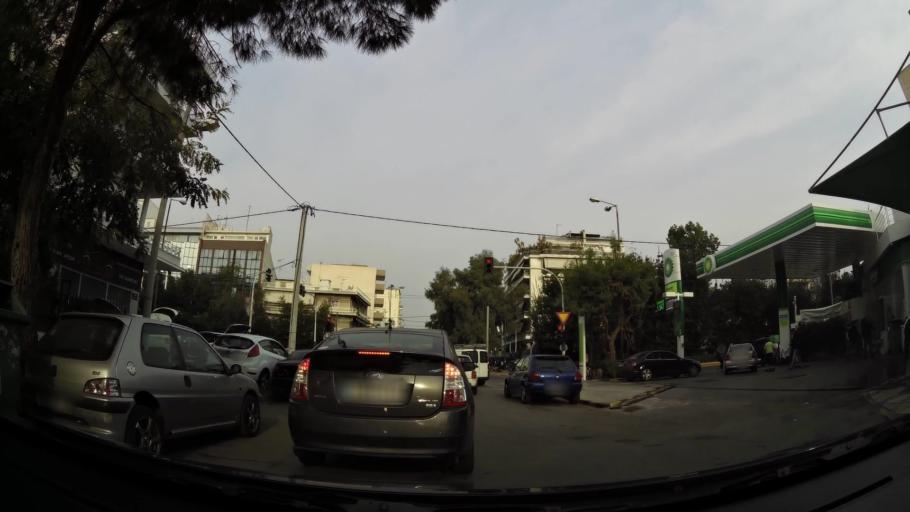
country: GR
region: Attica
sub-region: Nomarchia Athinas
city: Kallithea
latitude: 37.9478
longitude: 23.6896
